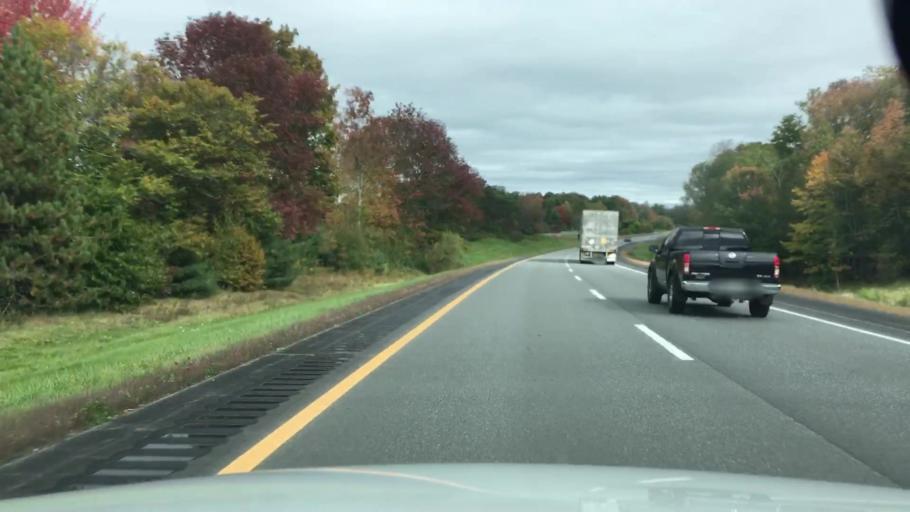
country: US
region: Maine
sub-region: Penobscot County
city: Newport
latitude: 44.8359
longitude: -69.3038
